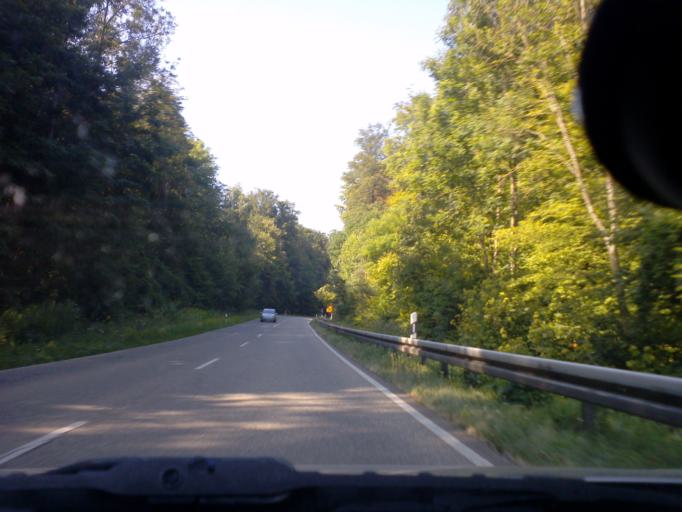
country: DE
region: Baden-Wuerttemberg
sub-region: Karlsruhe Region
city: Knittlingen
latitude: 49.0586
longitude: 8.7466
